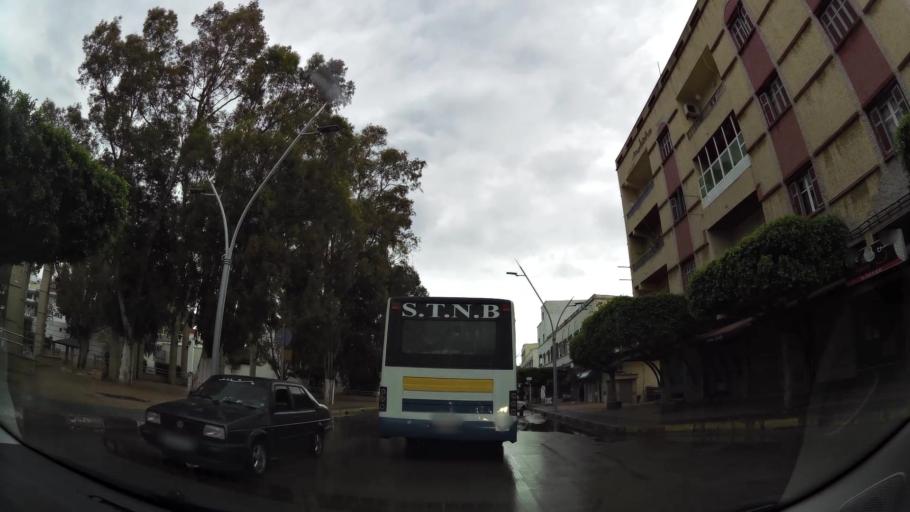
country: MA
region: Oriental
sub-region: Nador
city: Nador
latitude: 35.1542
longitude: -3.0031
